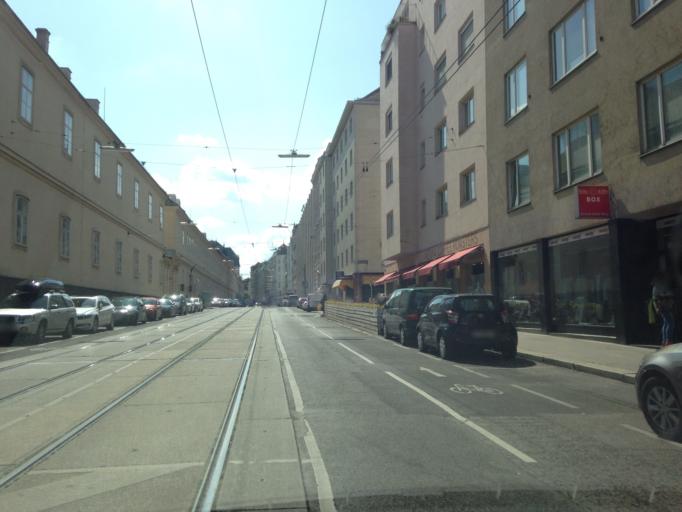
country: AT
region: Vienna
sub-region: Wien Stadt
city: Vienna
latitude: 48.2177
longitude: 16.3514
